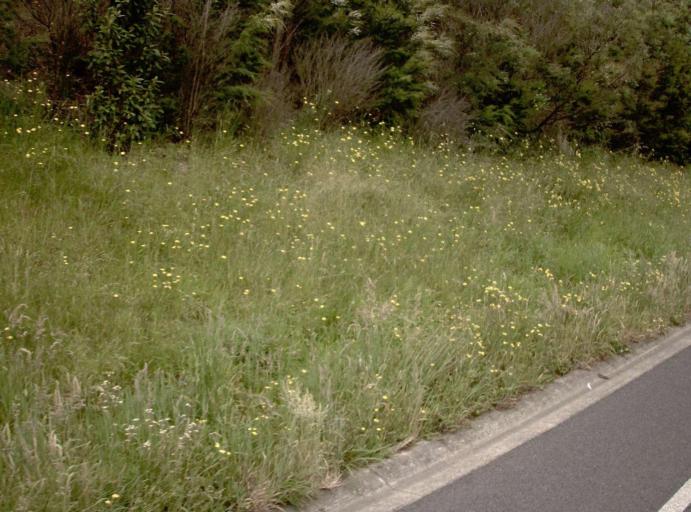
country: AU
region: Victoria
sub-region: Bass Coast
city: North Wonthaggi
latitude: -38.4093
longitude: 145.7644
